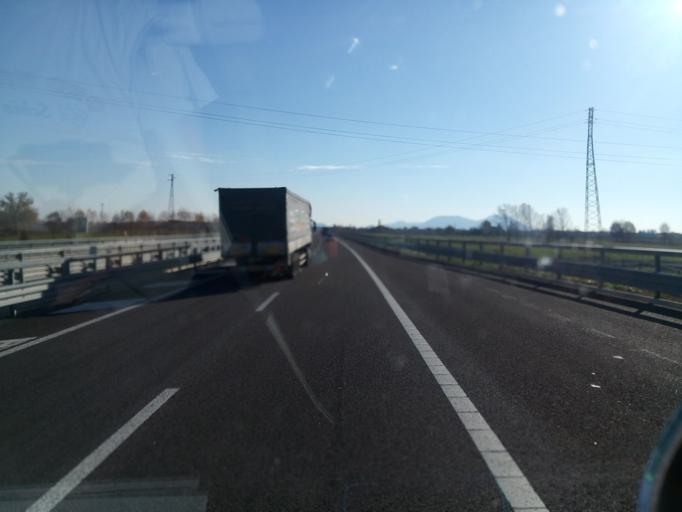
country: IT
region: Veneto
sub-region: Provincia di Vicenza
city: Longare
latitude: 45.4952
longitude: 11.6175
